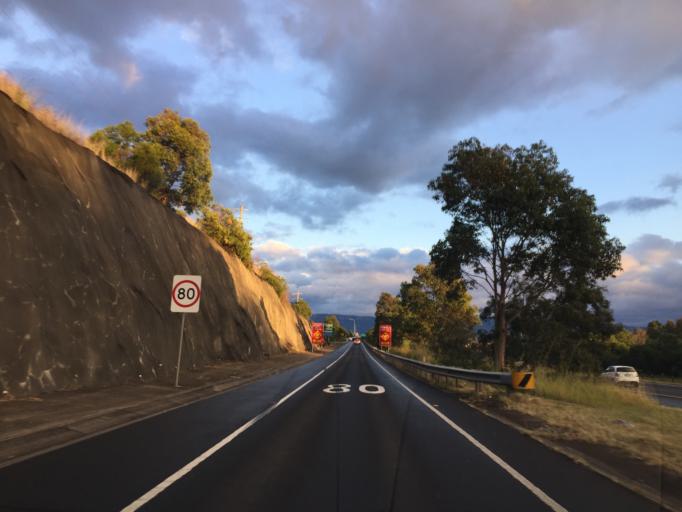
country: AU
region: New South Wales
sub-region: Shellharbour
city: Croom
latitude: -34.5749
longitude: 150.8253
